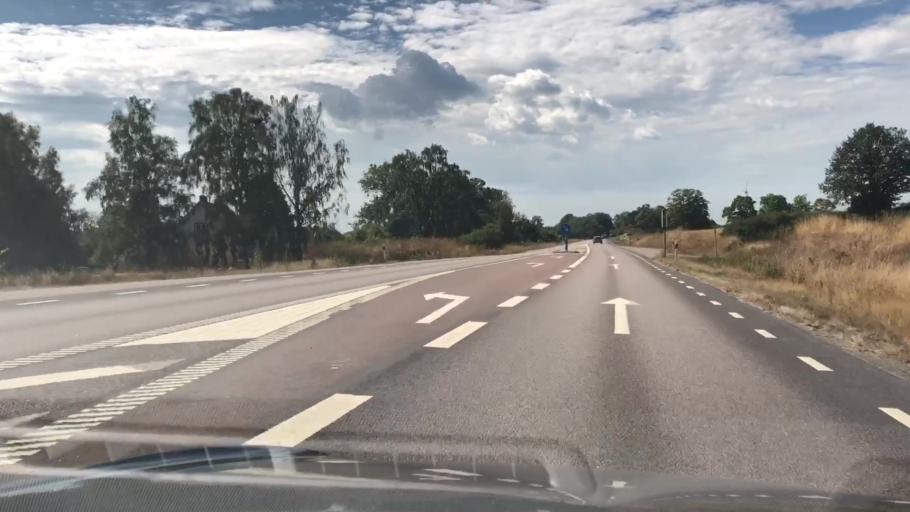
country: SE
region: Kalmar
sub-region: Torsas Kommun
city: Torsas
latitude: 56.4279
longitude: 16.0764
